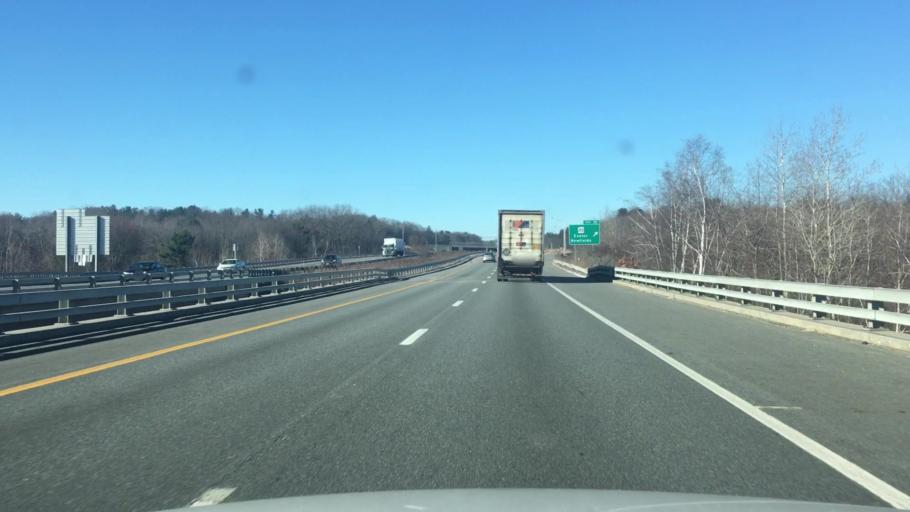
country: US
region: New Hampshire
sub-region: Rockingham County
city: Exeter
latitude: 43.0002
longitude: -70.9400
